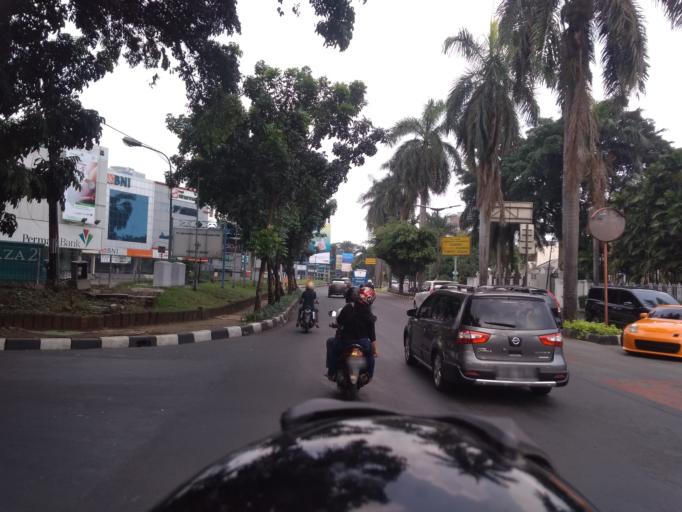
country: ID
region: Banten
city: South Tangerang
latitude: -6.2856
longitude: 106.7798
